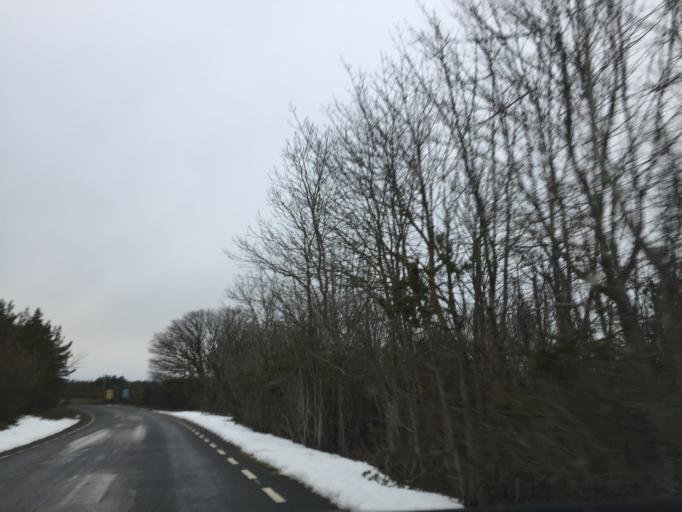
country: EE
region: Saare
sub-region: Kuressaare linn
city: Kuressaare
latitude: 58.5670
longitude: 22.3050
